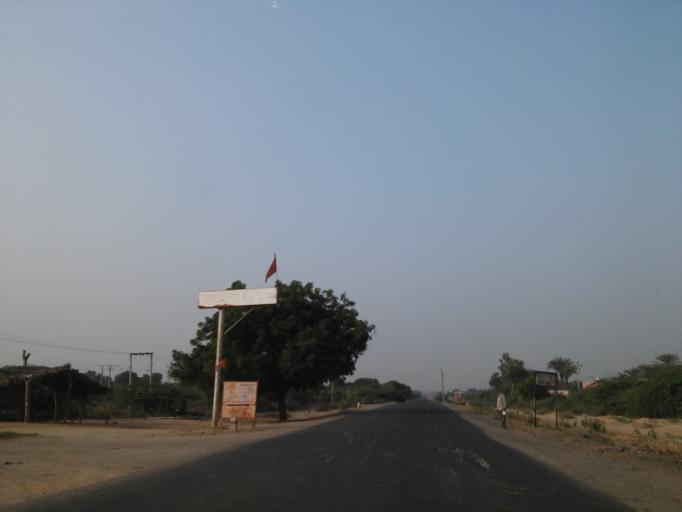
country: IN
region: Gujarat
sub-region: Kachchh
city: Bhachau
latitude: 23.3403
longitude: 70.2427
